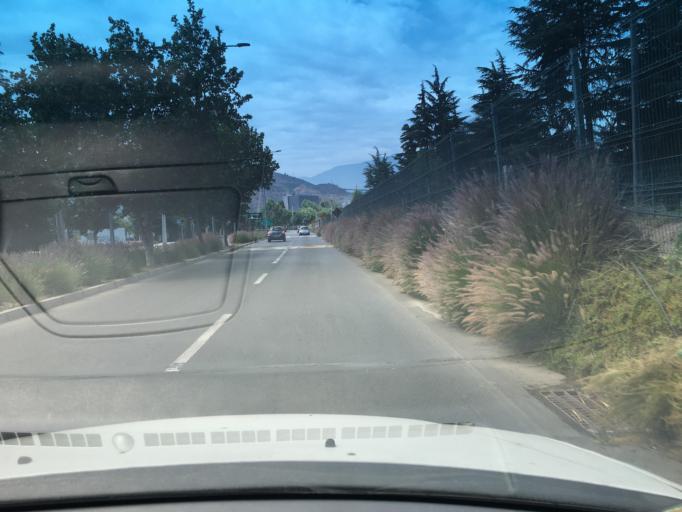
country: CL
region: Santiago Metropolitan
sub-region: Provincia de Santiago
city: Santiago
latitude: -33.3817
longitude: -70.6321
